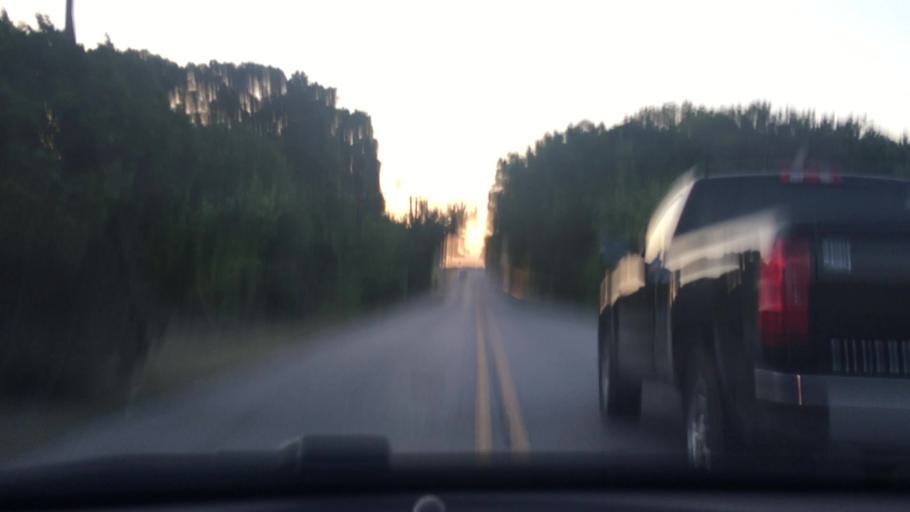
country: US
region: Texas
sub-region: Dallas County
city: Lancaster
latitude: 32.5609
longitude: -96.7764
